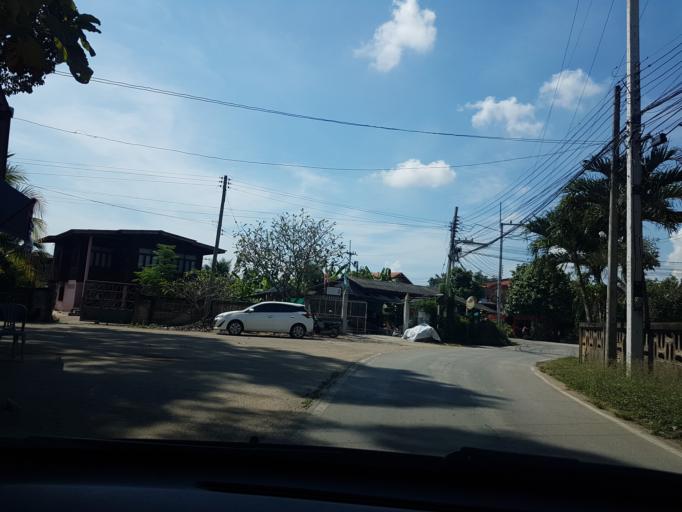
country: TH
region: Lampang
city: Ko Kha
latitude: 18.2079
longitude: 99.4010
